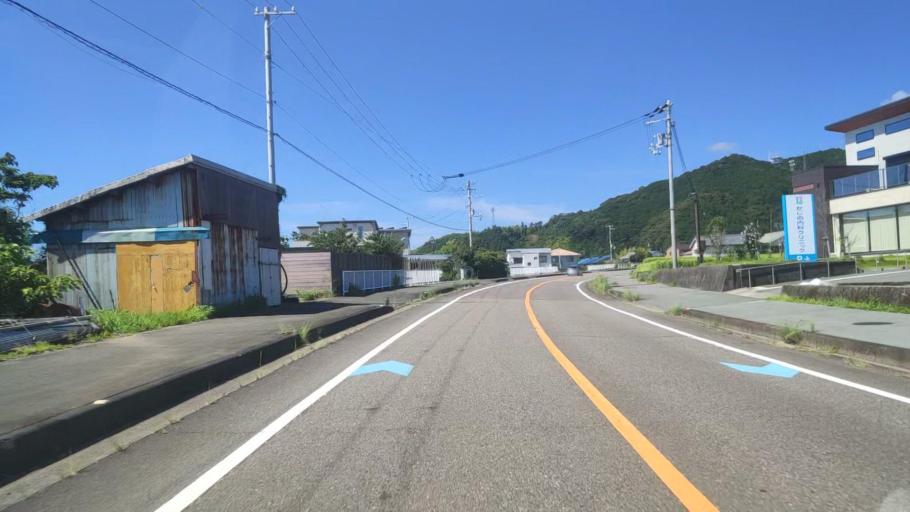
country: JP
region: Wakayama
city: Shingu
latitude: 33.7058
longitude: 135.9932
